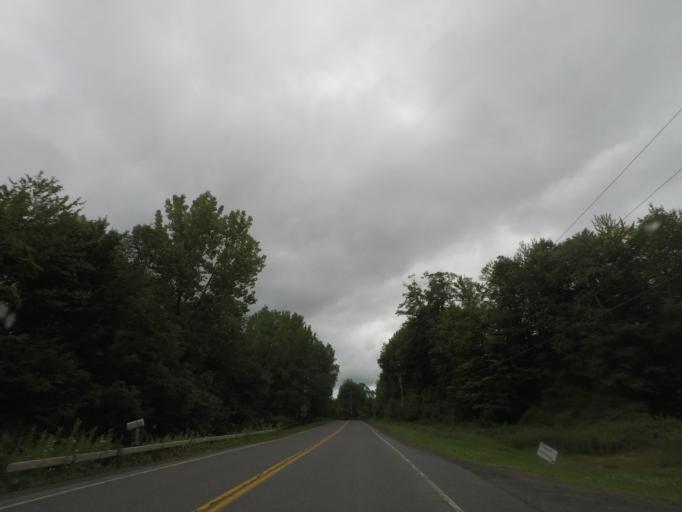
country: US
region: New York
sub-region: Rensselaer County
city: Poestenkill
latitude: 42.6878
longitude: -73.4890
